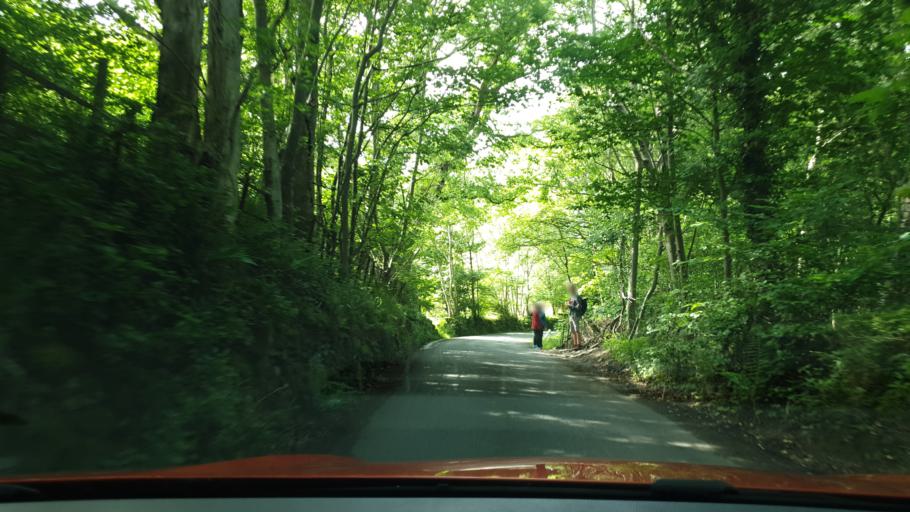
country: GB
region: England
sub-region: Cumbria
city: Penrith
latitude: 54.5794
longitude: -2.8536
